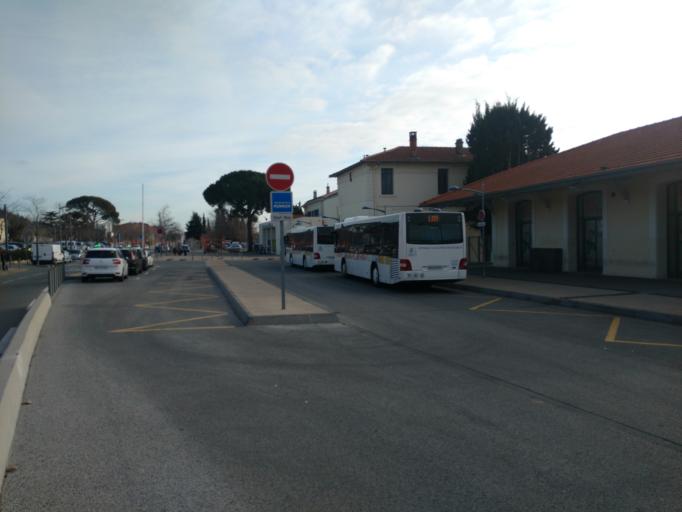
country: FR
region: Provence-Alpes-Cote d'Azur
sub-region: Departement du Var
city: Les Arcs
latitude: 43.4557
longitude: 6.4813
